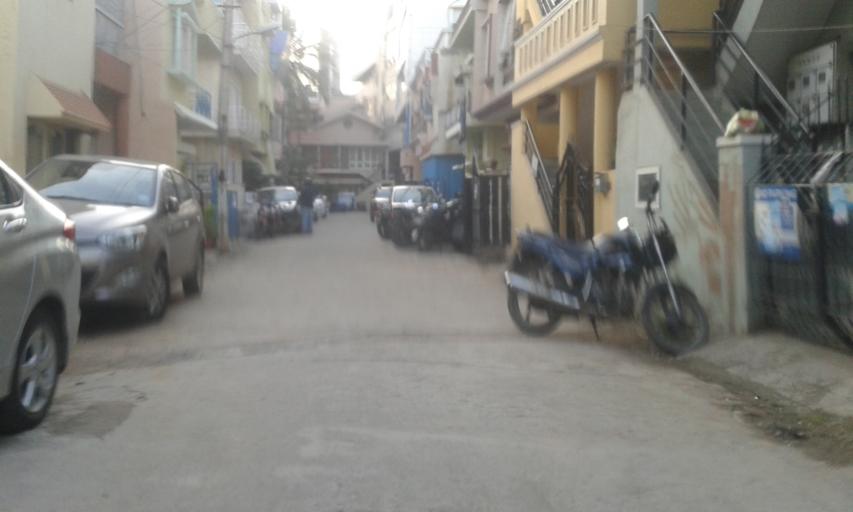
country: IN
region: Karnataka
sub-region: Bangalore Urban
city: Bangalore
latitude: 12.9630
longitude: 77.6427
